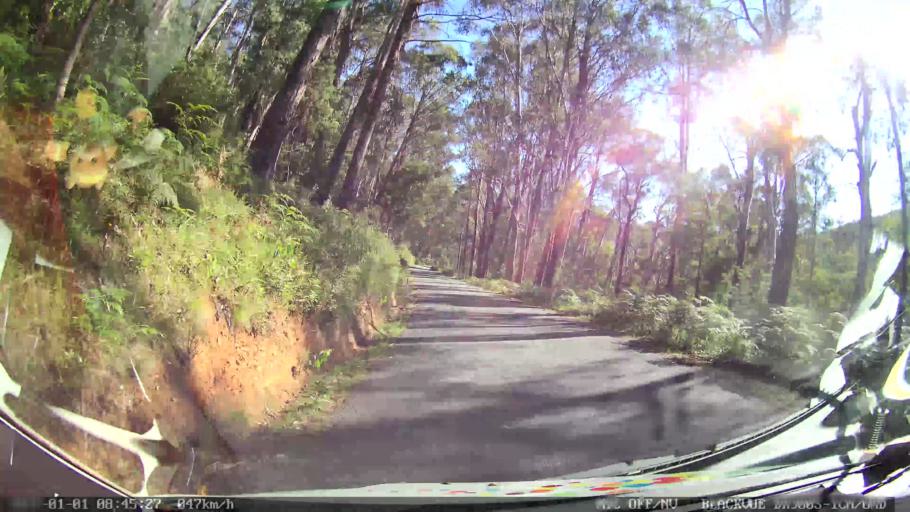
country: AU
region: New South Wales
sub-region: Snowy River
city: Jindabyne
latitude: -36.3055
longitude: 148.1886
